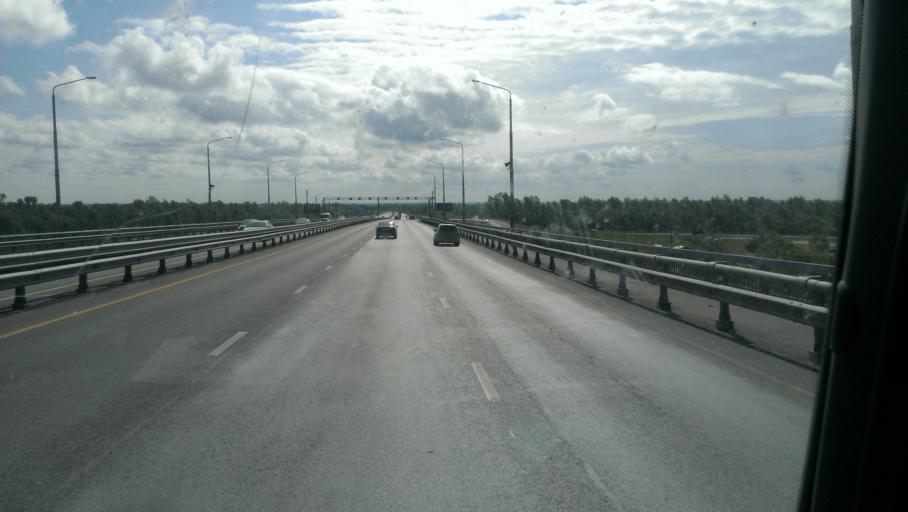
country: RU
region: Altai Krai
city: Zaton
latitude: 53.3215
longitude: 83.8088
